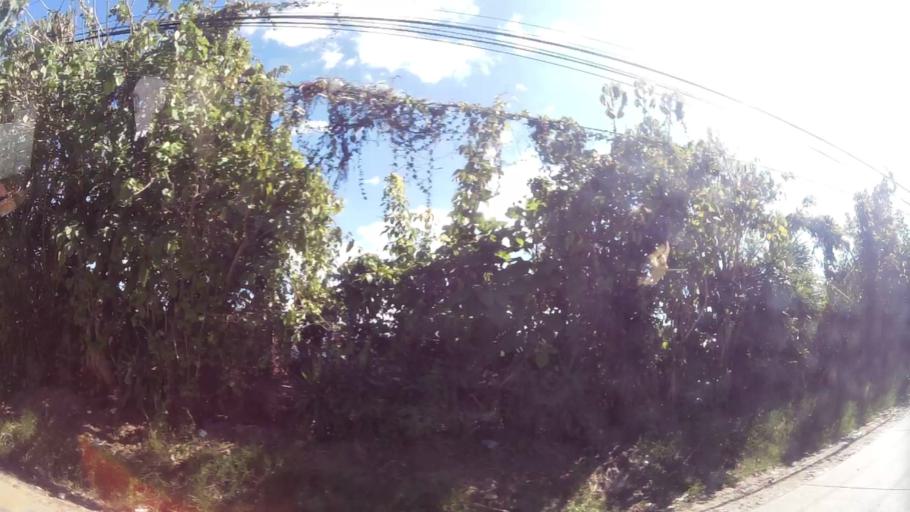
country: GT
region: Guatemala
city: Petapa
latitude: 14.4990
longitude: -90.5625
